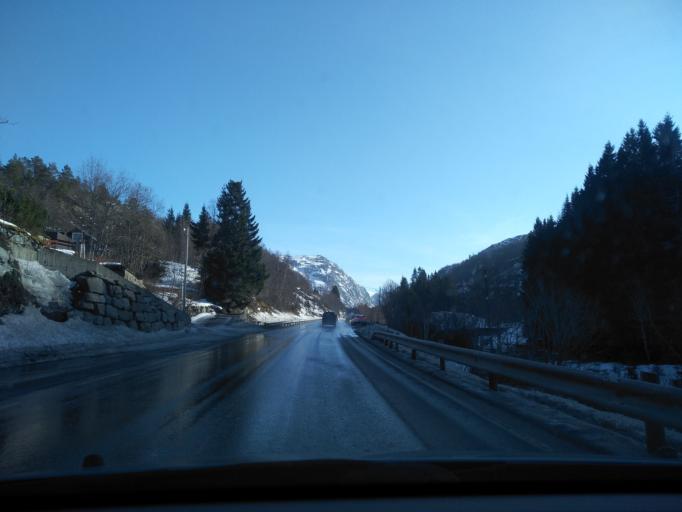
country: NO
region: Hordaland
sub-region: Odda
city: Odda
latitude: 59.8986
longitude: 6.6290
